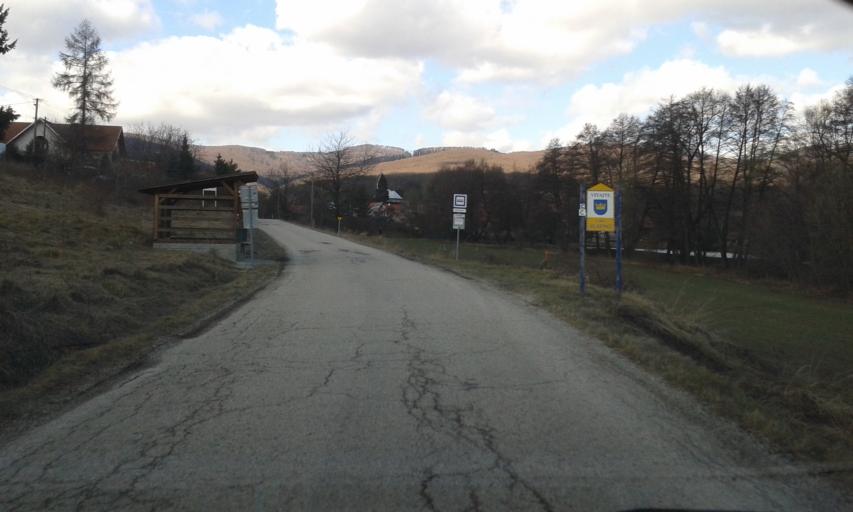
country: SK
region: Nitriansky
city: Zlate Moravce
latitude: 48.4593
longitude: 18.3178
